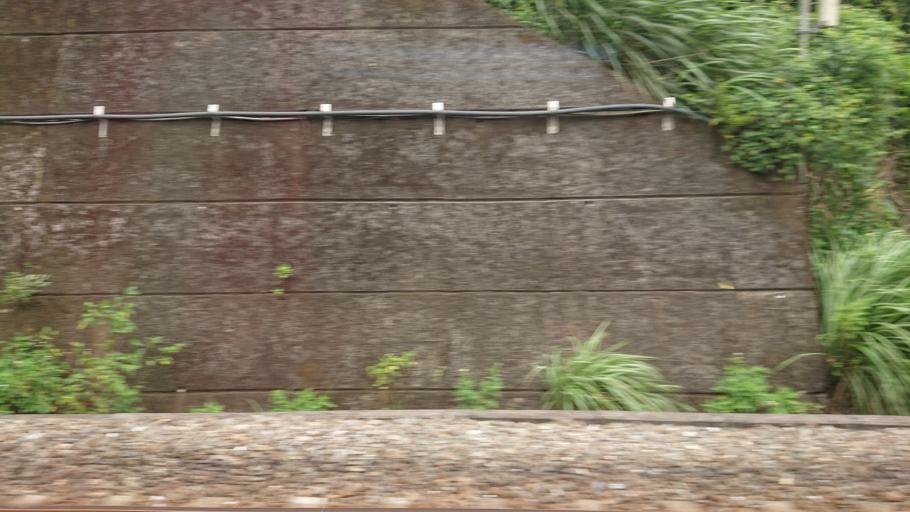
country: TW
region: Taiwan
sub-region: Keelung
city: Keelung
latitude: 25.0051
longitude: 121.9577
